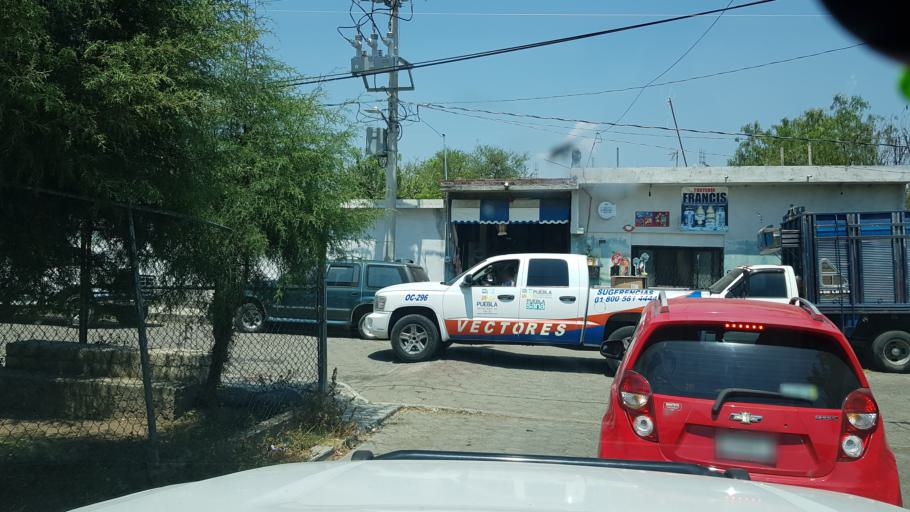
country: MX
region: Puebla
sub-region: Huaquechula
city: Cacaloxuchitl
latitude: 18.7924
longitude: -98.4672
